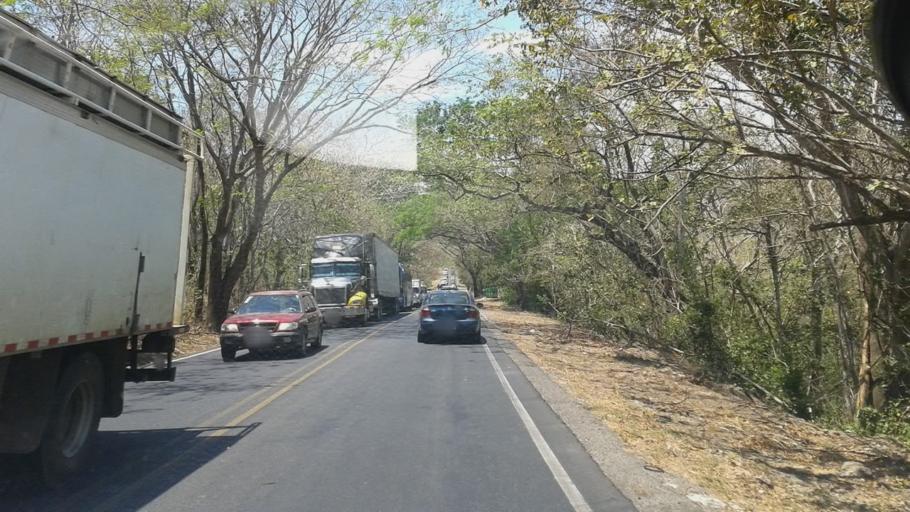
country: CR
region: Puntarenas
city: Miramar
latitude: 10.0874
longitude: -84.8365
